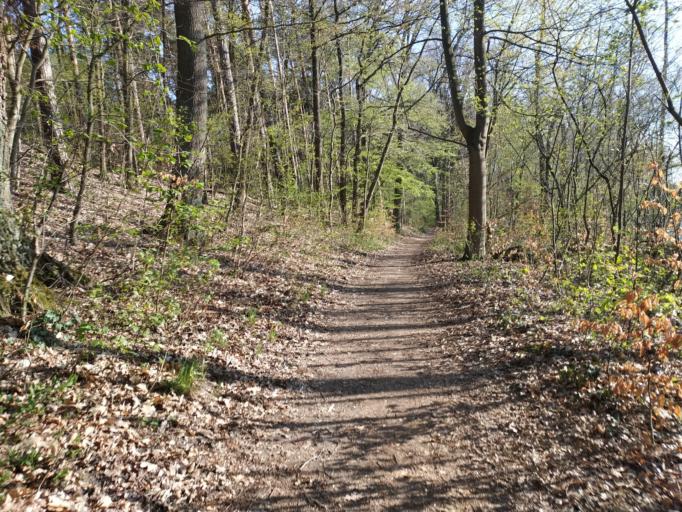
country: DE
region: Brandenburg
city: Strausberg
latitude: 52.5777
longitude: 13.8331
